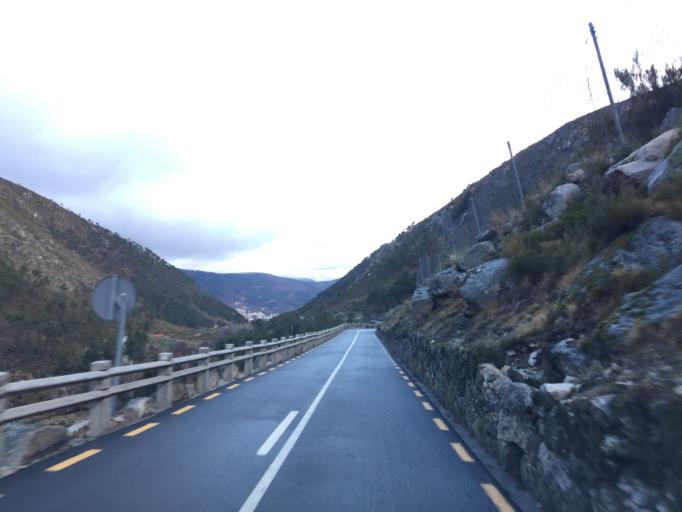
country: PT
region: Guarda
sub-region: Manteigas
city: Manteigas
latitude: 40.3547
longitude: -7.5583
